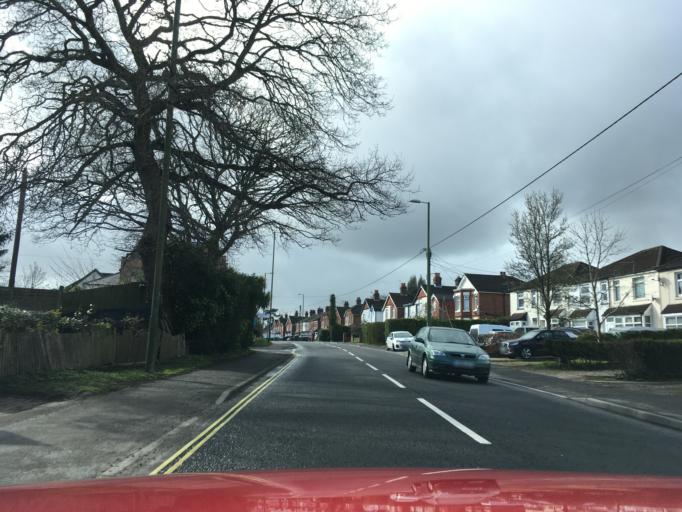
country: GB
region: England
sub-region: Hampshire
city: Chandlers Ford
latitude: 50.9768
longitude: -1.3871
